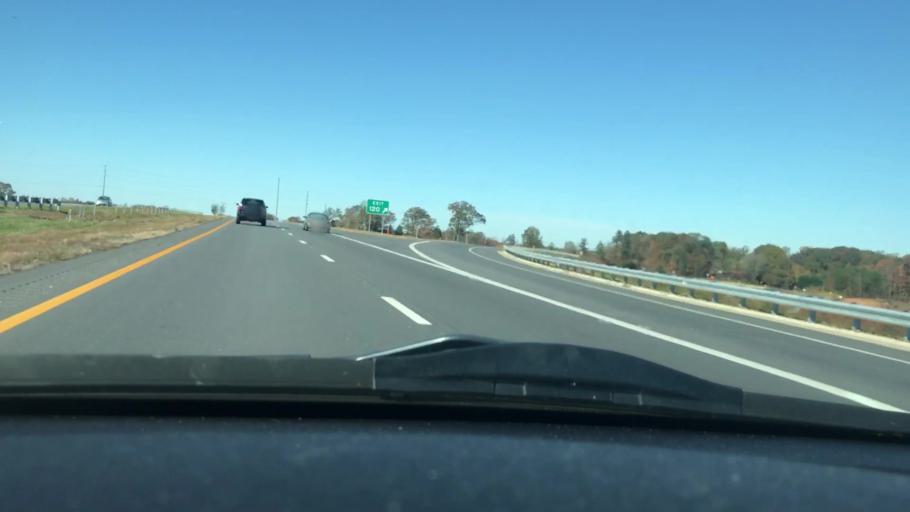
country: US
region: North Carolina
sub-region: Guilford County
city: Summerfield
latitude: 36.2438
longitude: -79.9198
